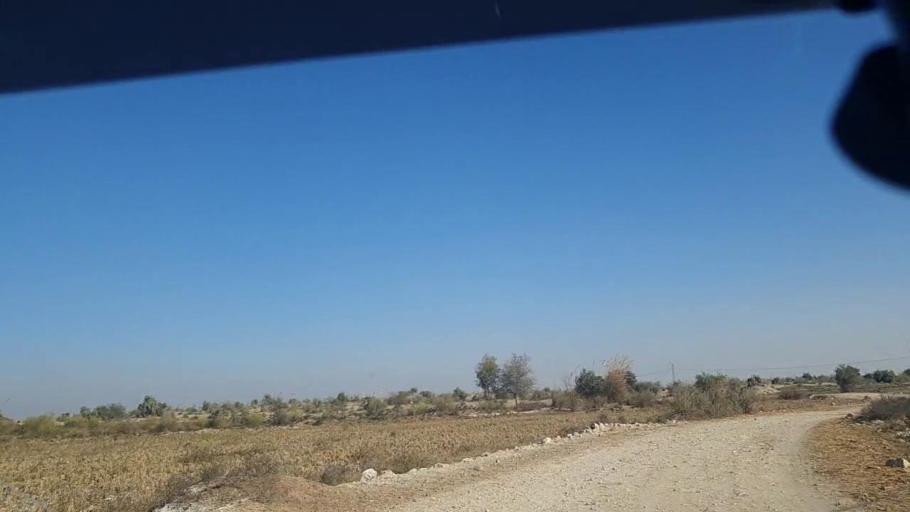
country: PK
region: Sindh
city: Khanpur
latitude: 27.6483
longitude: 69.3933
